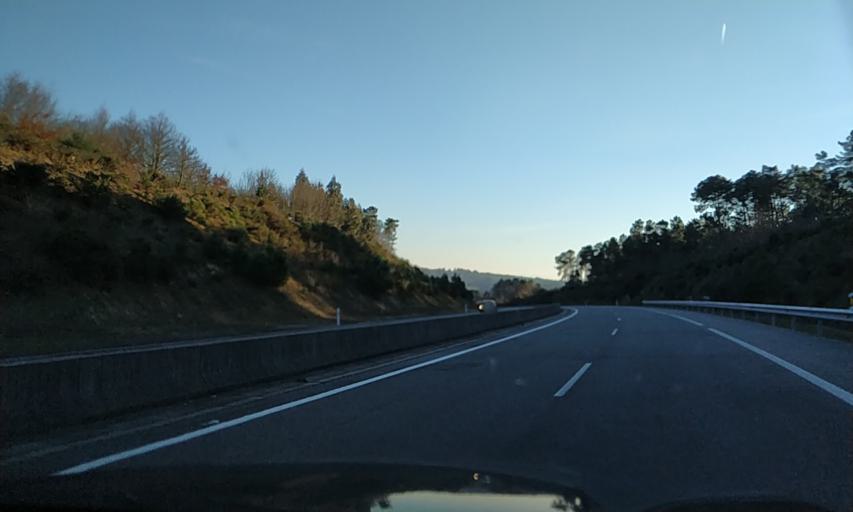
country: ES
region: Galicia
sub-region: Provincia de Ourense
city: Pinor
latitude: 42.4772
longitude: -8.0261
